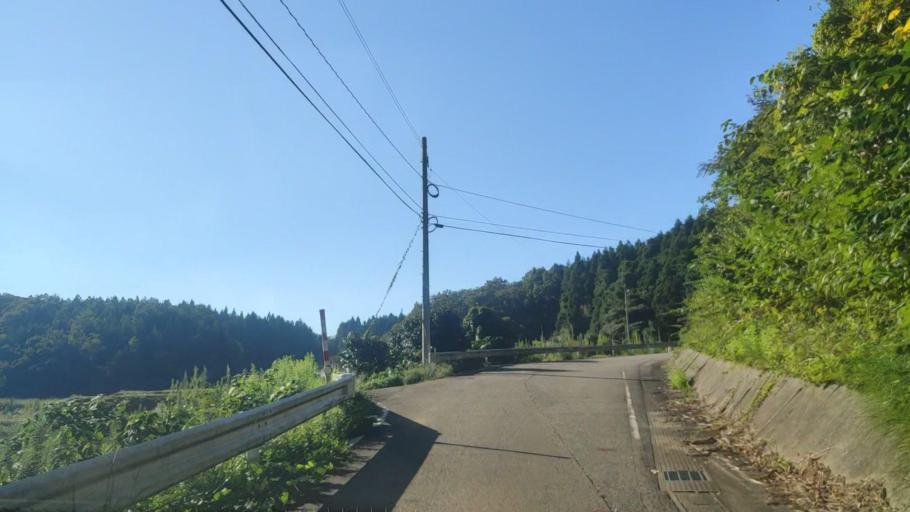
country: JP
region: Ishikawa
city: Nanao
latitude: 37.1289
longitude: 136.8945
